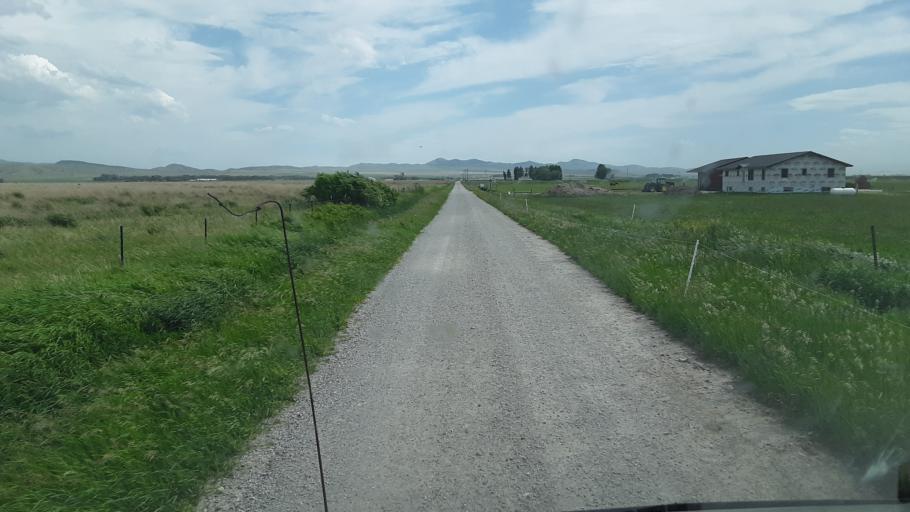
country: US
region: Montana
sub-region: Broadwater County
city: Townsend
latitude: 46.1817
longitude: -111.4720
